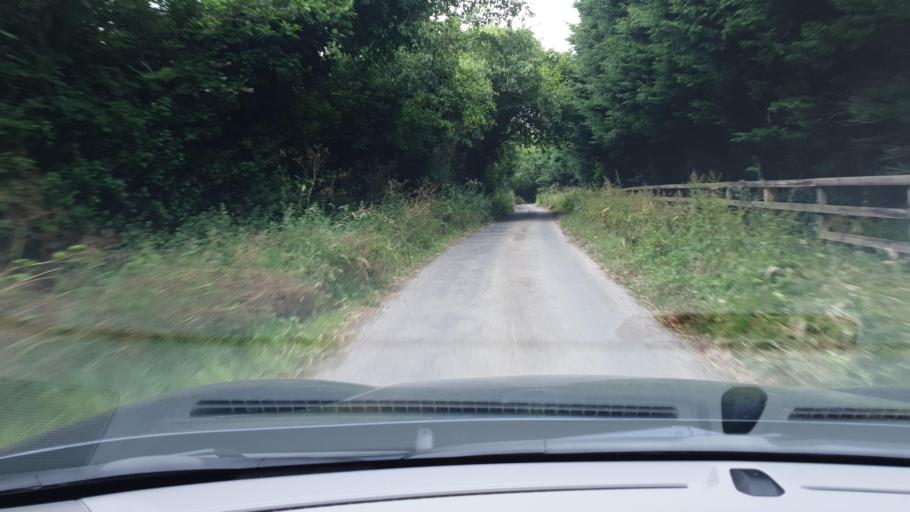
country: IE
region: Leinster
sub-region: An Mhi
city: Ashbourne
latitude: 53.5369
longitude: -6.3890
